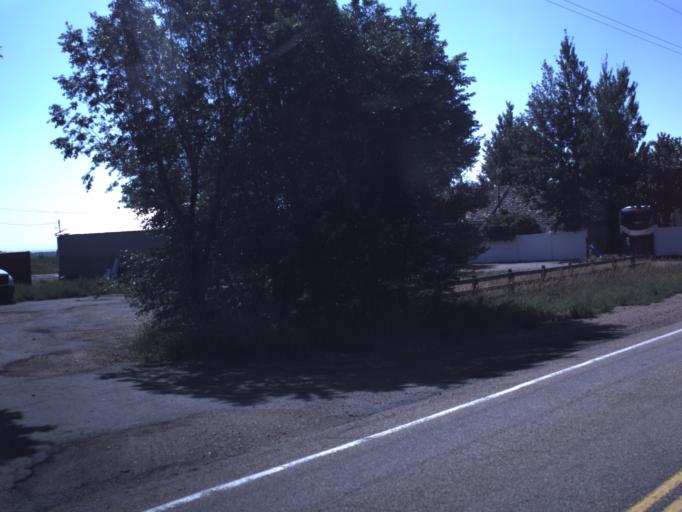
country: US
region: Utah
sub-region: Duchesne County
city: Duchesne
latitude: 40.3548
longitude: -110.2753
